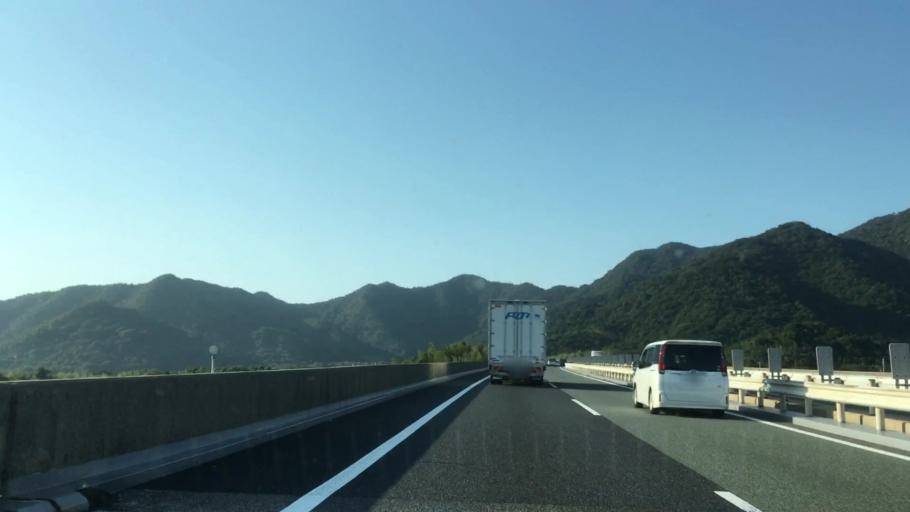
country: JP
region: Yamaguchi
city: Ogori-shimogo
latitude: 34.0941
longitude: 131.4551
